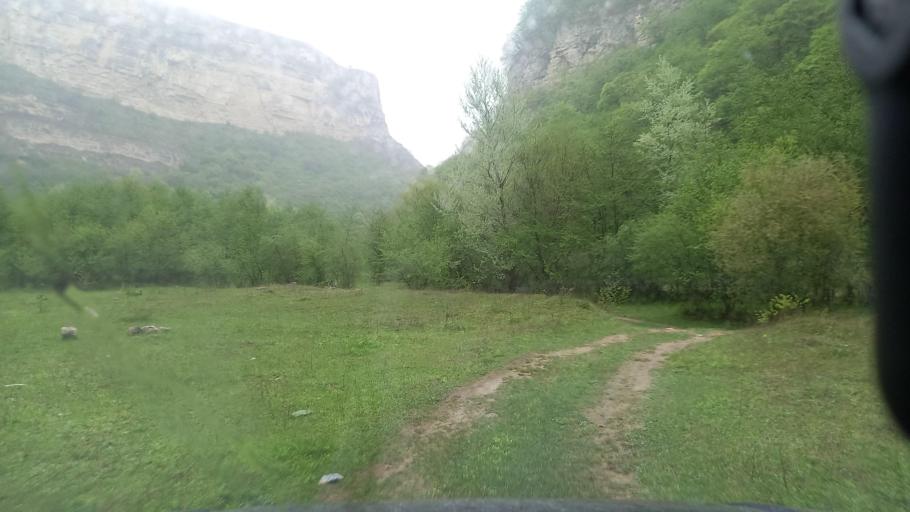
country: RU
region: Kabardino-Balkariya
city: Gundelen
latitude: 43.5891
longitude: 43.1226
